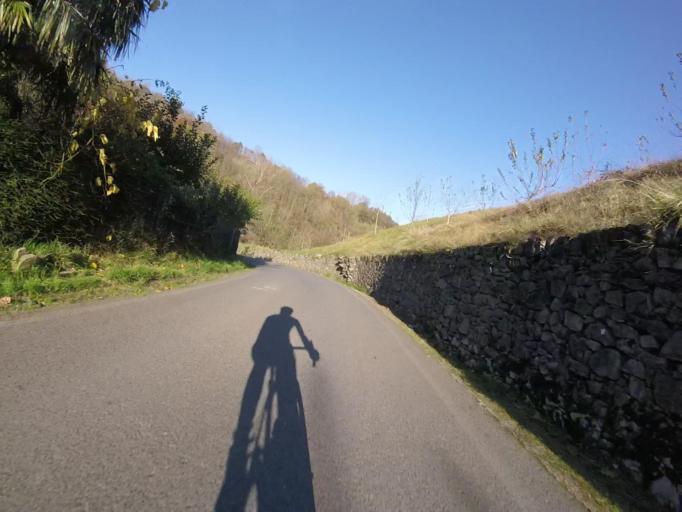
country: ES
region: Navarre
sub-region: Provincia de Navarra
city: Lesaka
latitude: 43.2396
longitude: -1.7030
